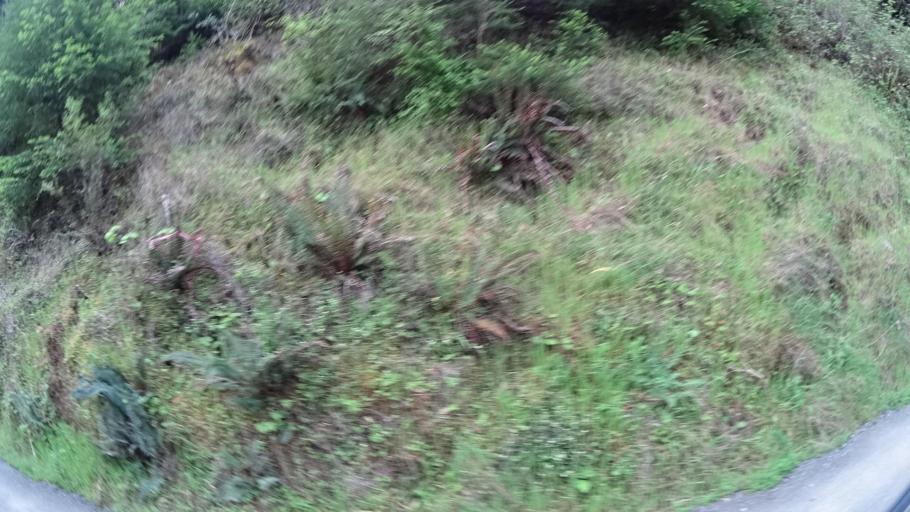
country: US
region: California
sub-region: Humboldt County
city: Redway
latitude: 40.3200
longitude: -123.8317
